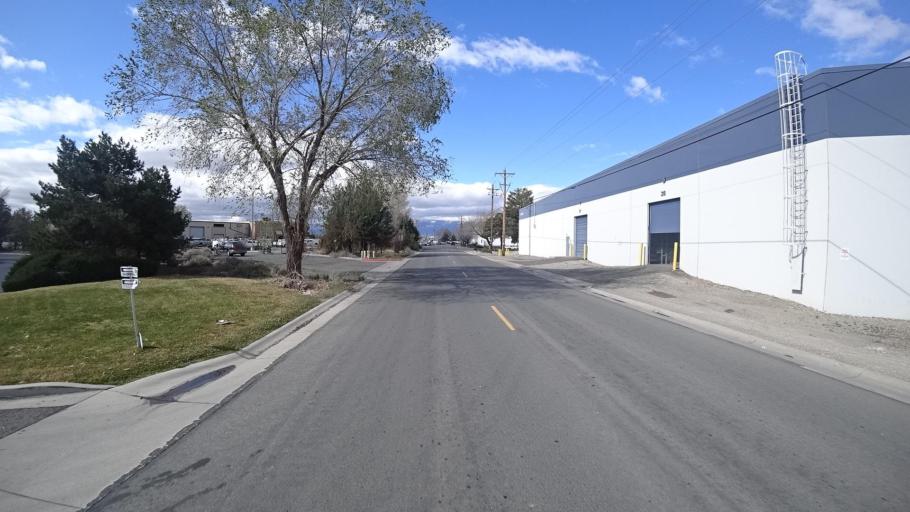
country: US
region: Nevada
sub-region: Washoe County
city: Sparks
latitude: 39.5251
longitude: -119.7187
